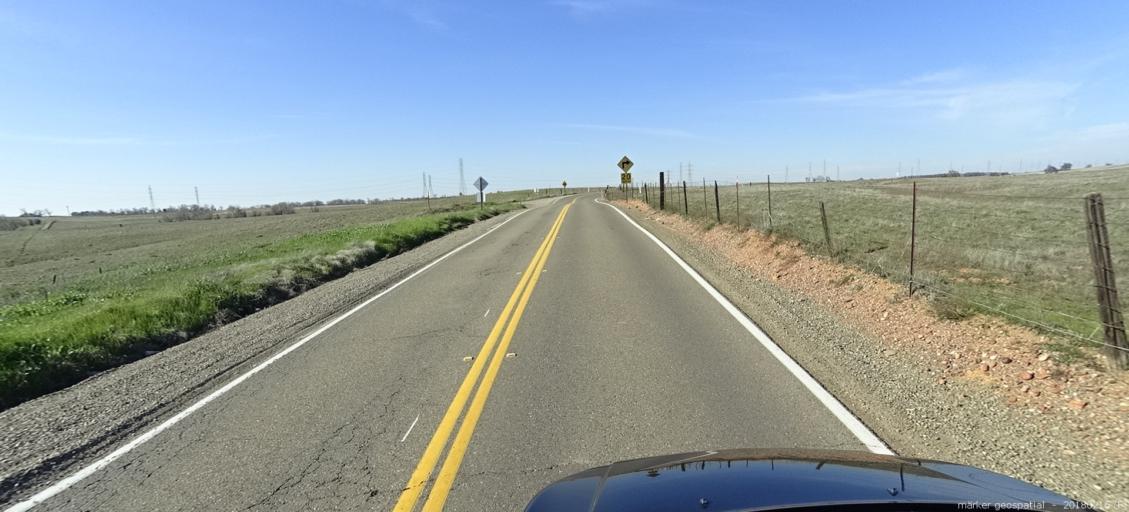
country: US
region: California
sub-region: Sacramento County
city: Folsom
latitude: 38.6054
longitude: -121.1409
